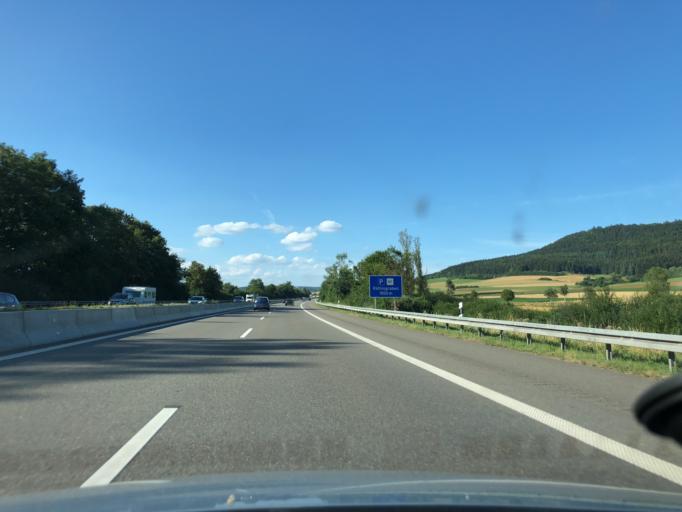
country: DE
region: Baden-Wuerttemberg
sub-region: Freiburg Region
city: Geisingen
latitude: 47.9506
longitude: 8.6189
